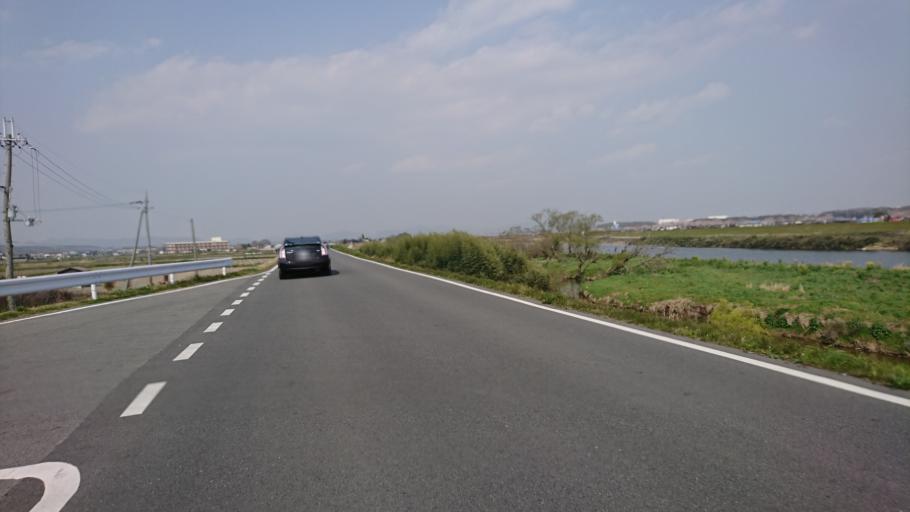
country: JP
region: Hyogo
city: Ono
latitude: 34.8639
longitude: 134.9160
